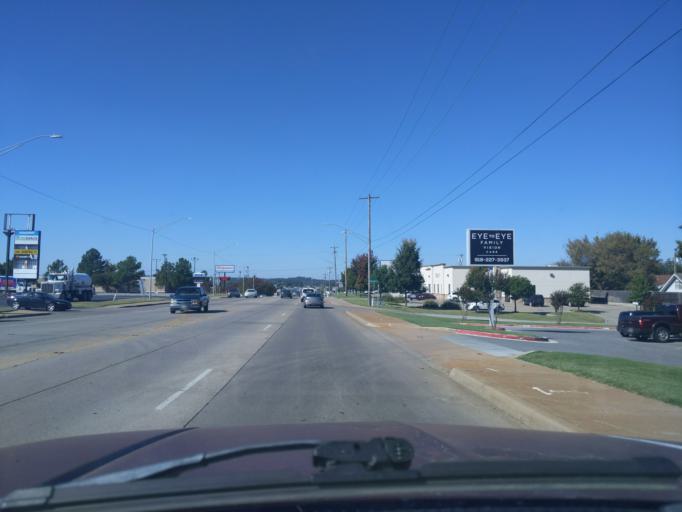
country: US
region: Oklahoma
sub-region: Creek County
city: Sapulpa
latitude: 35.9885
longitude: -96.0993
